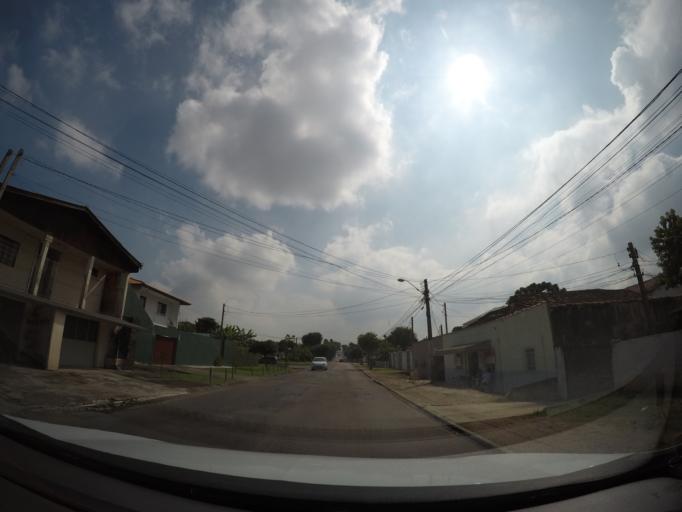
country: BR
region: Parana
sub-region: Sao Jose Dos Pinhais
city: Sao Jose dos Pinhais
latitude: -25.4922
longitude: -49.2546
